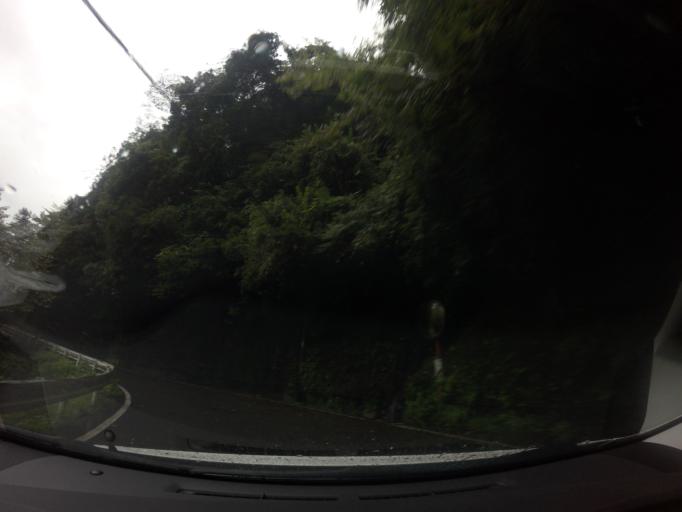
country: JP
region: Wakayama
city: Koya
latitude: 34.0634
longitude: 135.7462
